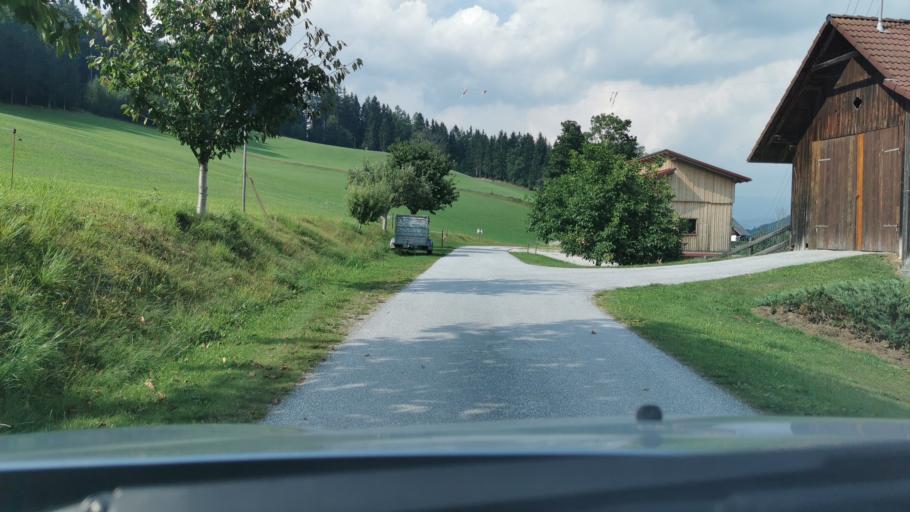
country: AT
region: Styria
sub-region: Politischer Bezirk Weiz
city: Strallegg
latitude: 47.4122
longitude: 15.6893
